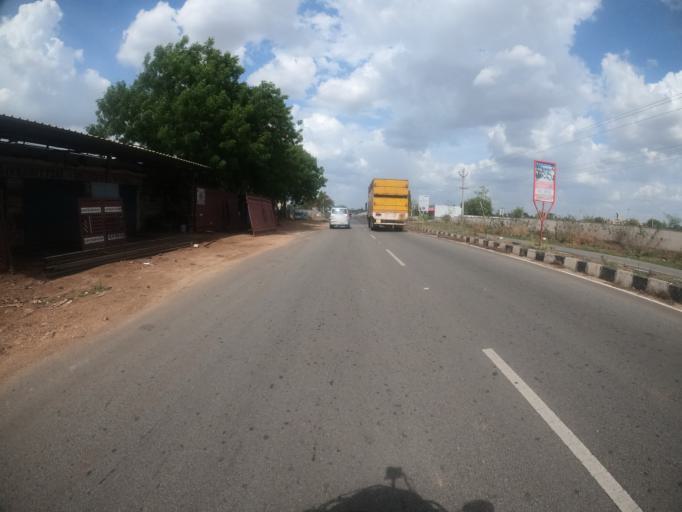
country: IN
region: Telangana
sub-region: Rangareddi
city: Sriramnagar
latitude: 17.3313
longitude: 78.2900
